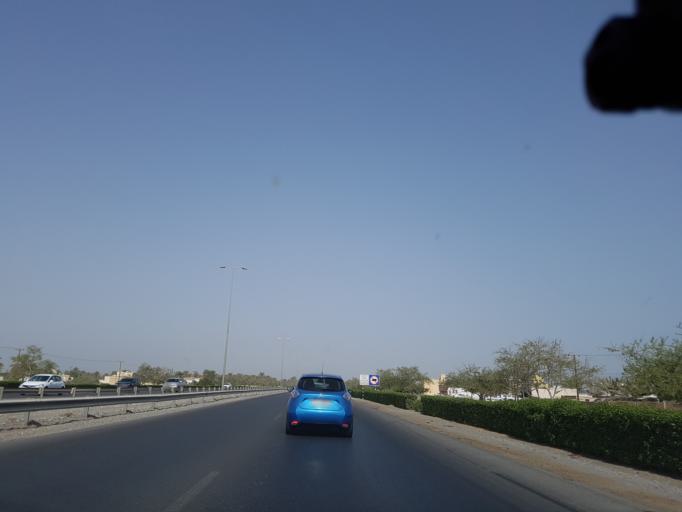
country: OM
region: Al Batinah
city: Barka'
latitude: 23.7371
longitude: 57.6585
